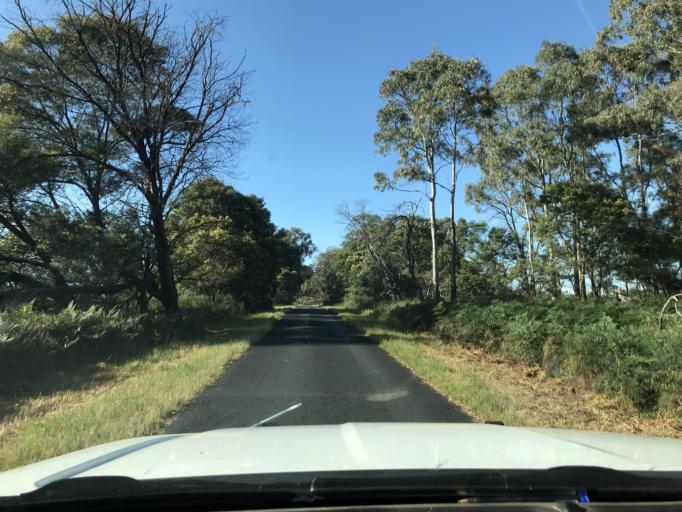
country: AU
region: South Australia
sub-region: Wattle Range
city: Penola
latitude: -37.2014
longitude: 140.9714
